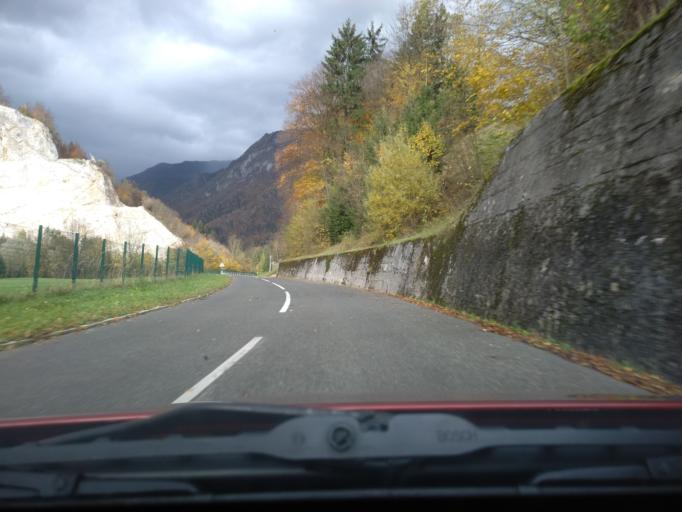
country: SI
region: Kamnik
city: Mekinje
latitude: 46.2750
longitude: 14.6123
